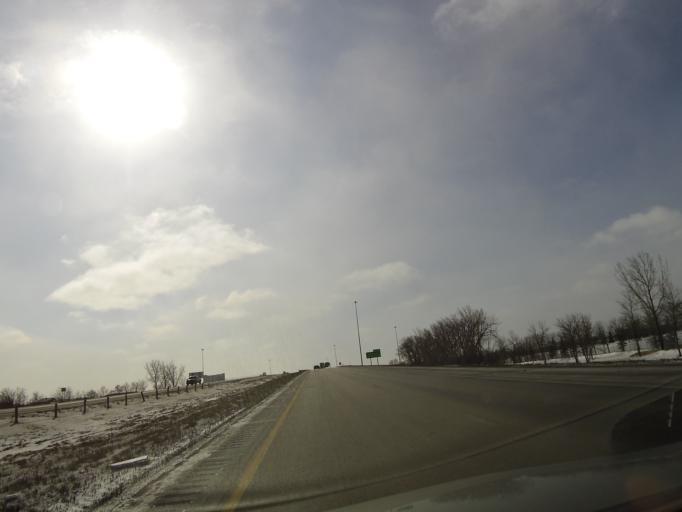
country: US
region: North Dakota
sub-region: Grand Forks County
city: Grand Forks
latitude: 47.9219
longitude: -97.0936
